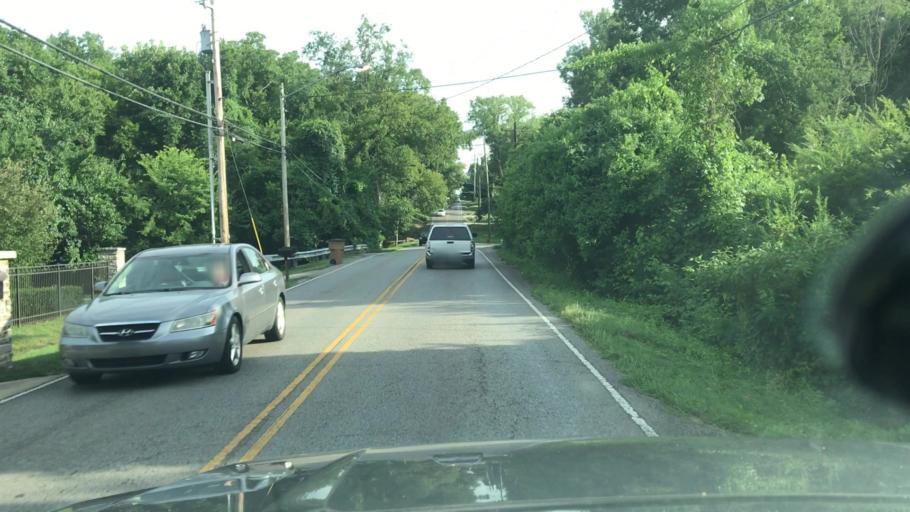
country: US
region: Tennessee
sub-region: Davidson County
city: Belle Meade
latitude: 36.1150
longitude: -86.8367
